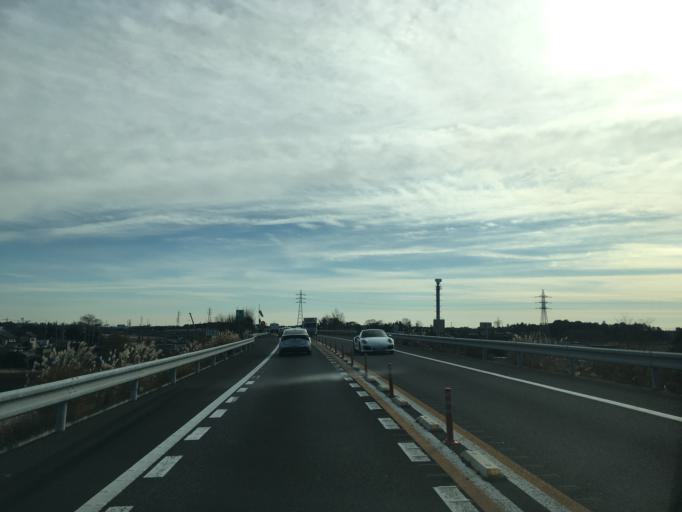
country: JP
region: Ibaraki
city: Naka
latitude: 36.0449
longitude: 140.1078
